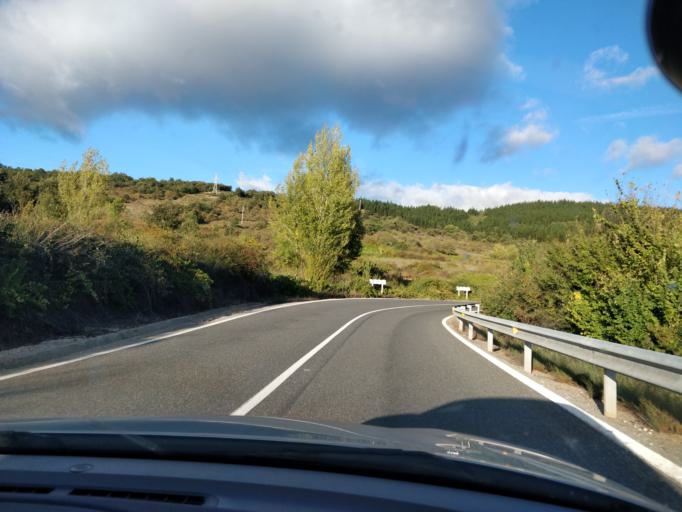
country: ES
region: Castille and Leon
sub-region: Provincia de Leon
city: Borrenes
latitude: 42.4980
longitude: -6.7207
